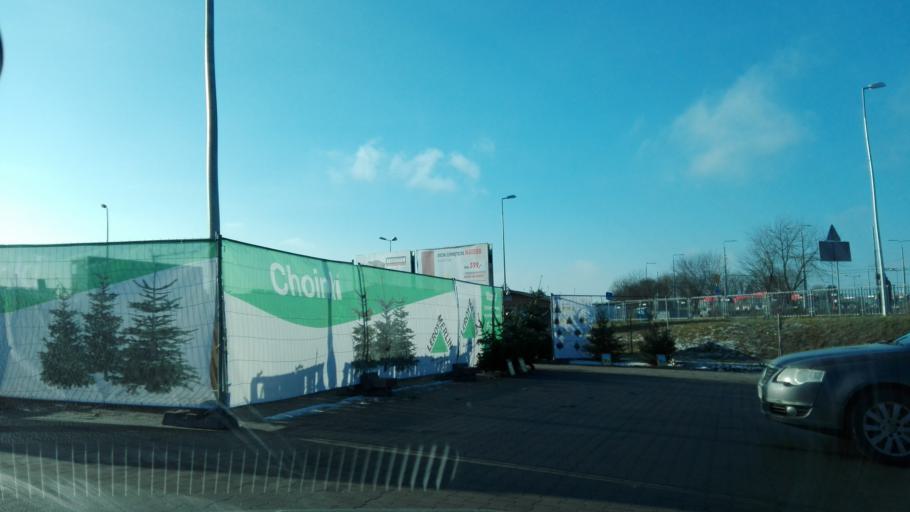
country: PL
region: Lublin Voivodeship
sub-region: Powiat lubelski
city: Kozubszczyzna
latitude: 51.2304
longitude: 22.4828
